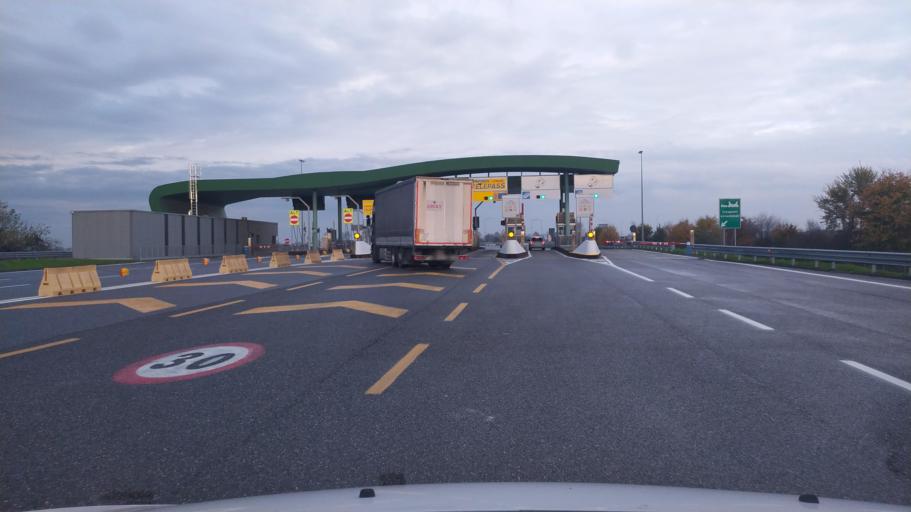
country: IT
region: Lombardy
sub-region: Provincia di Bergamo
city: Calcio
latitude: 45.4973
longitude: 9.8305
